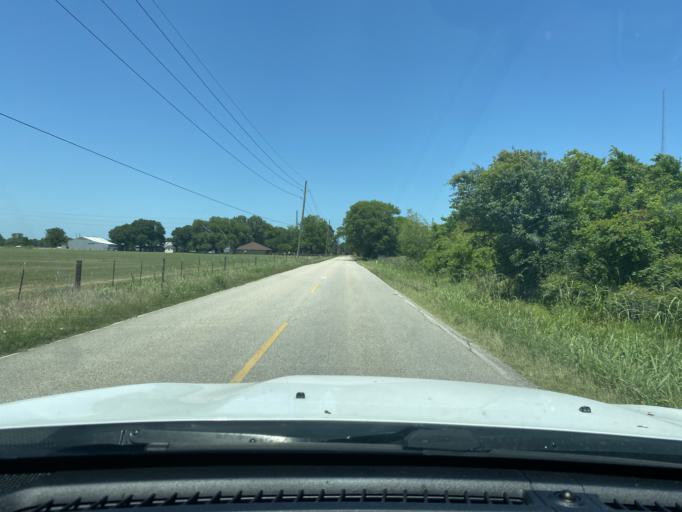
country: US
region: Texas
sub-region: Waller County
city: Waller
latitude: 30.0177
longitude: -95.8487
